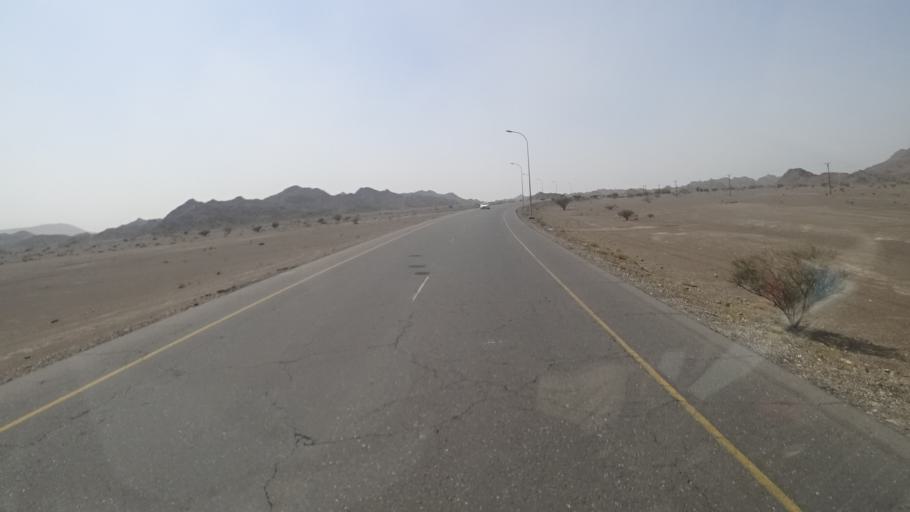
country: OM
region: Ash Sharqiyah
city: Ibra'
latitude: 22.6152
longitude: 58.3422
